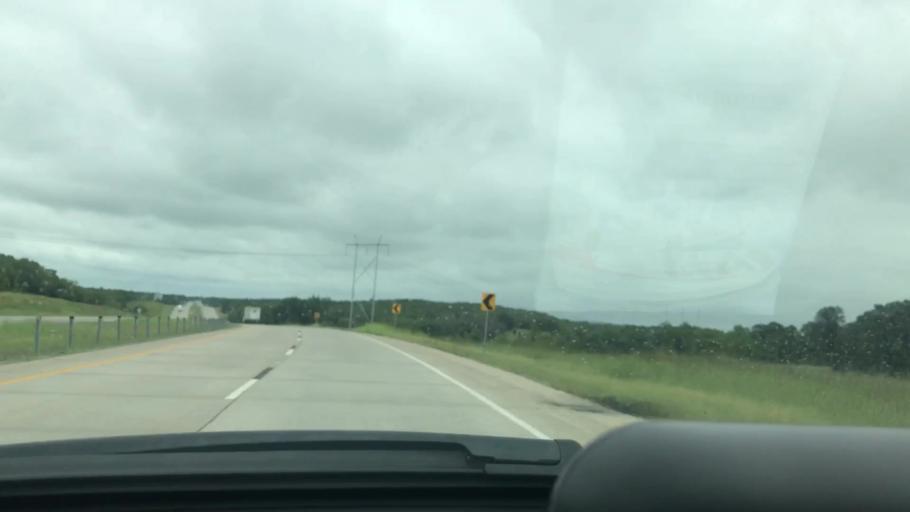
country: US
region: Oklahoma
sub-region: Pittsburg County
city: McAlester
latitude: 34.6921
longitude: -95.9118
